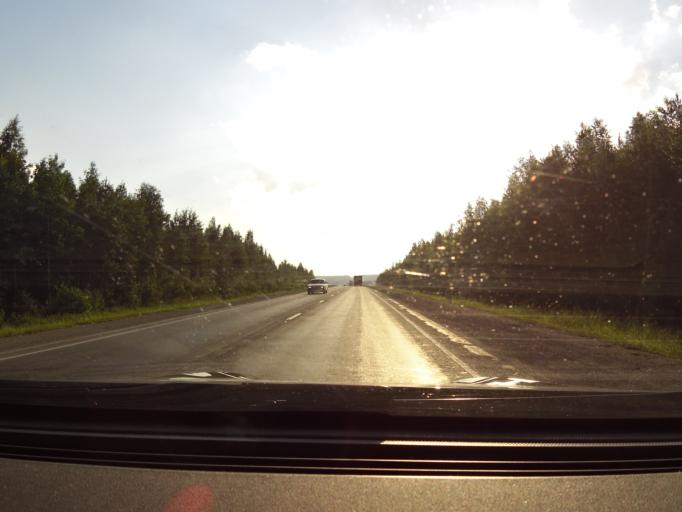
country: RU
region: Sverdlovsk
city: Revda
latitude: 56.8268
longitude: 59.9121
